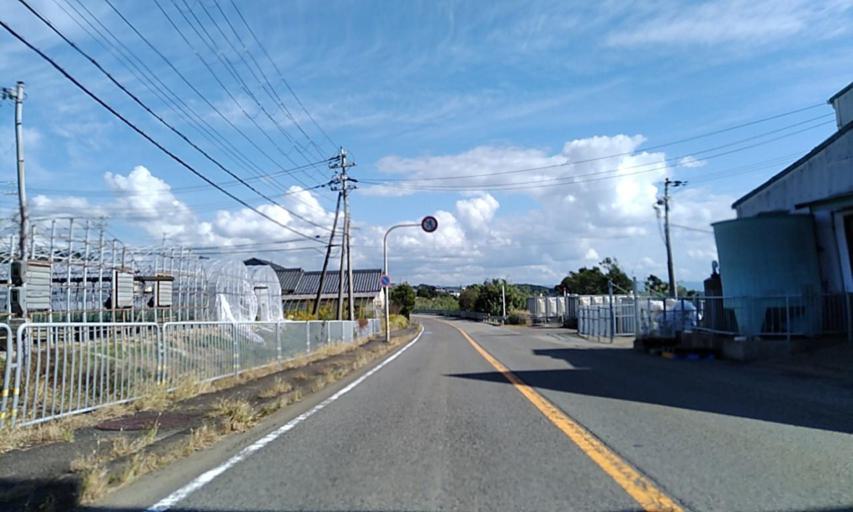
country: JP
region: Wakayama
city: Tanabe
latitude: 33.7837
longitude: 135.2690
